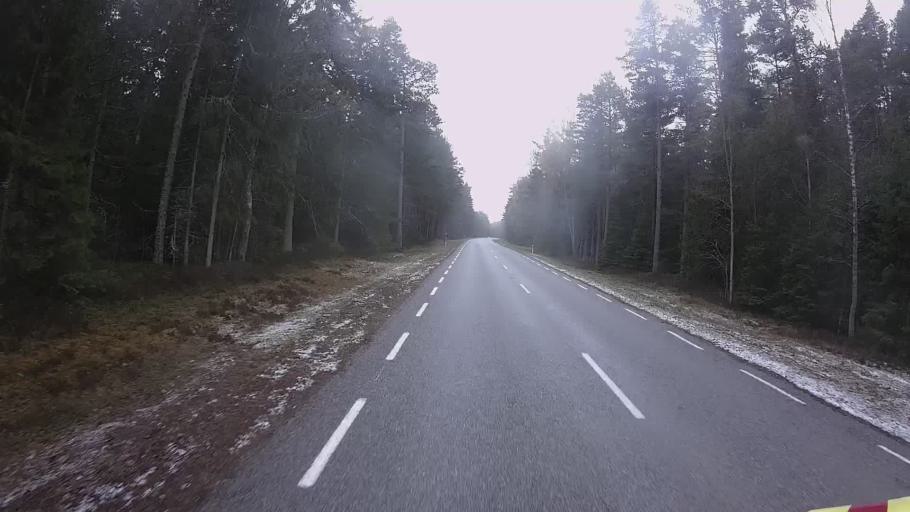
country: EE
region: Hiiumaa
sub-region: Kaerdla linn
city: Kardla
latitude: 59.0635
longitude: 22.6858
